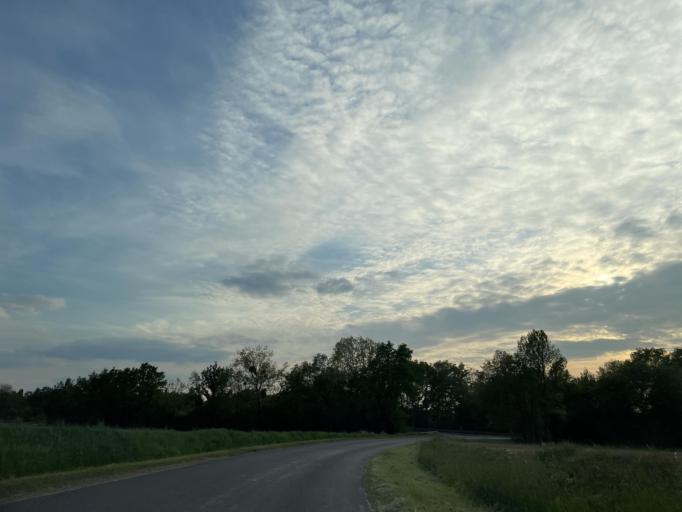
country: FR
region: Ile-de-France
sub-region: Departement de Seine-et-Marne
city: Bouleurs
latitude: 48.8934
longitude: 2.9106
